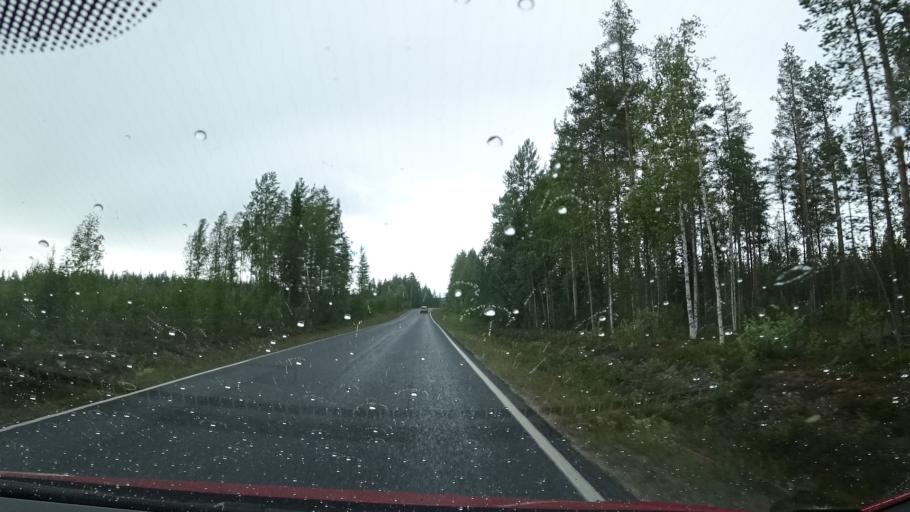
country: FI
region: Kainuu
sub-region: Kehys-Kainuu
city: Kuhmo
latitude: 63.9806
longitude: 29.2624
